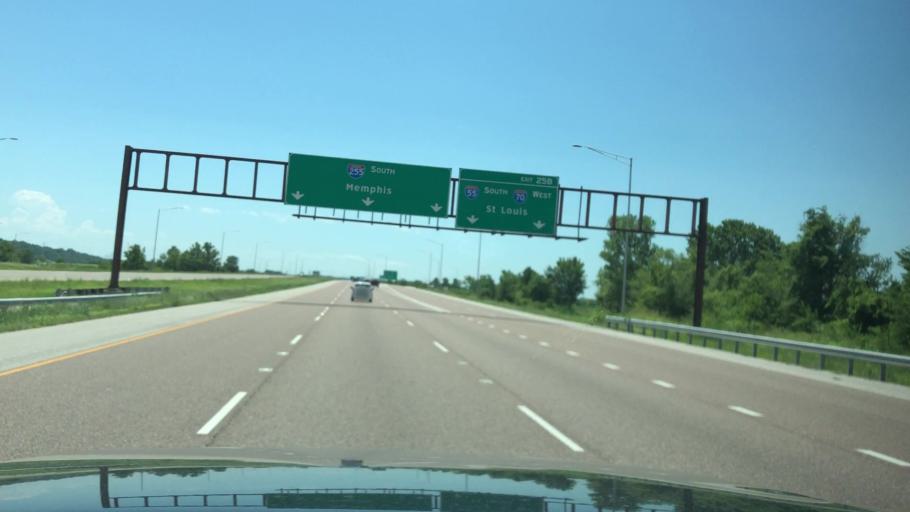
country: US
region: Illinois
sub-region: Saint Clair County
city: Caseyville
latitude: 38.6816
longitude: -90.0303
